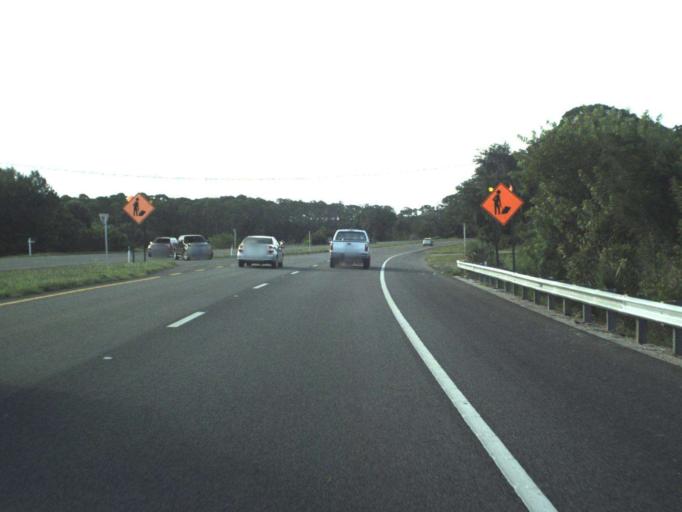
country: US
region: Florida
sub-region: Volusia County
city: Ponce Inlet
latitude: 29.0894
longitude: -80.9701
